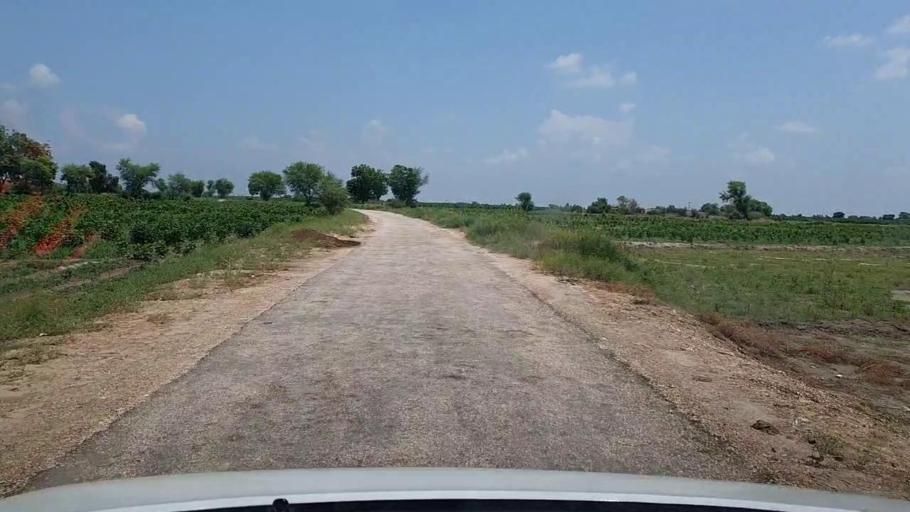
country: PK
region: Sindh
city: Bhiria
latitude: 26.9753
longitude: 68.2100
